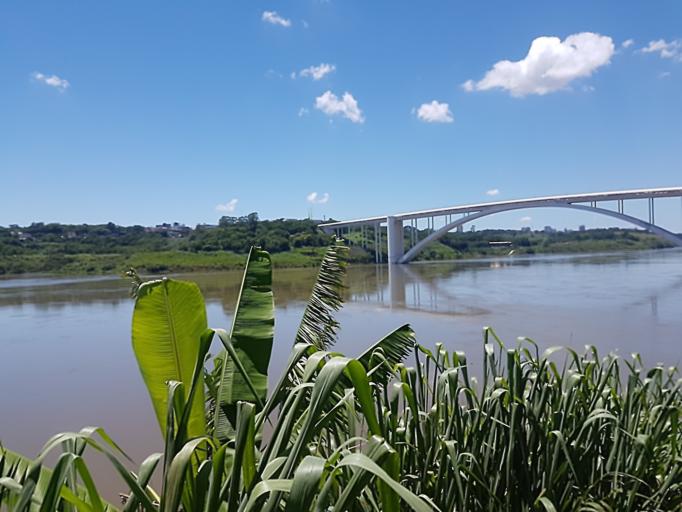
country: PY
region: Alto Parana
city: Ciudad del Este
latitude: -25.5053
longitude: -54.6032
